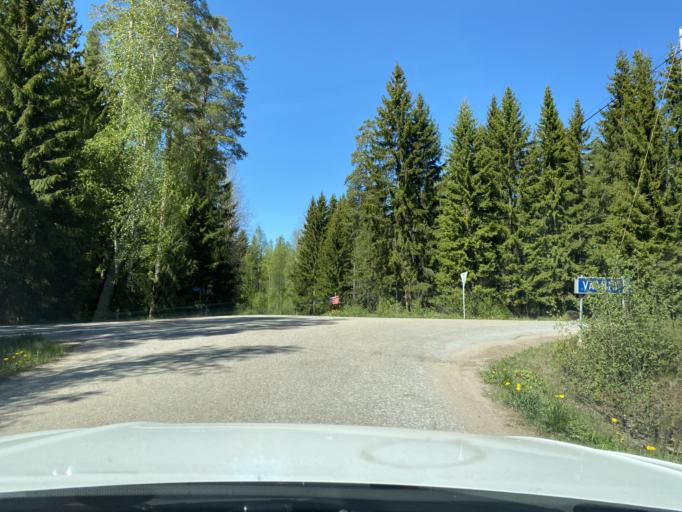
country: FI
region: Satakunta
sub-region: Rauma
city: Kiukainen
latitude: 61.1333
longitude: 21.9875
